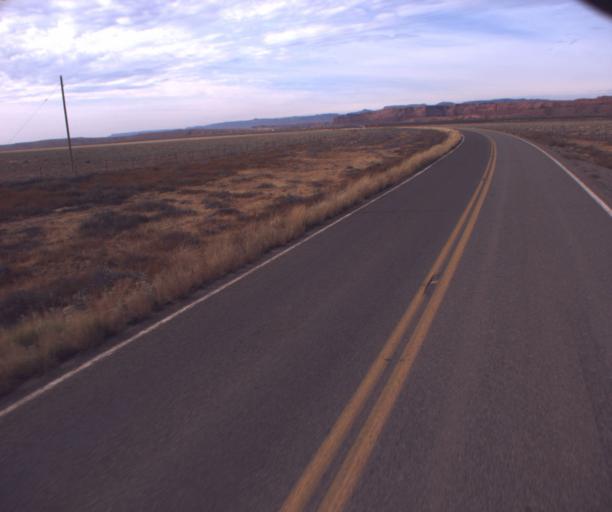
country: US
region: Arizona
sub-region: Apache County
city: Many Farms
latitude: 36.4637
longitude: -109.6002
